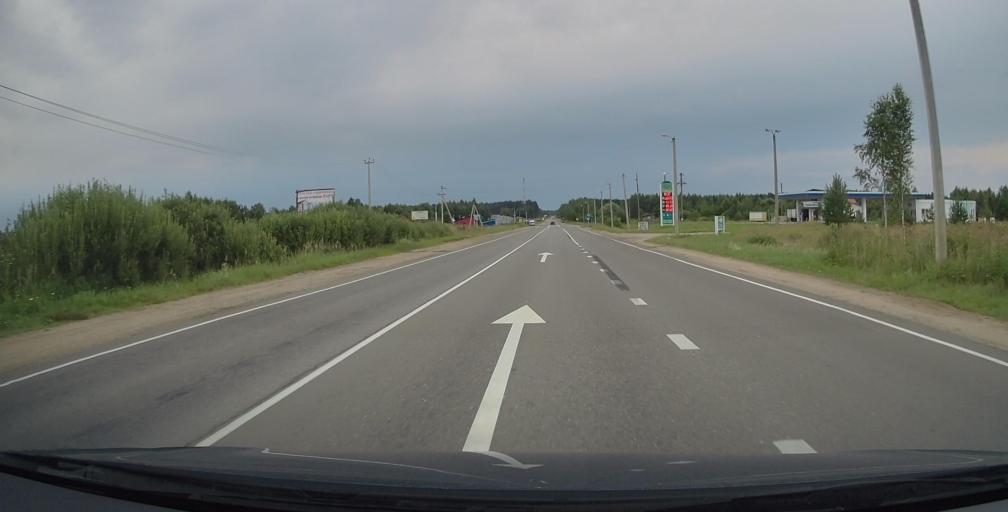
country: RU
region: Tverskaya
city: Kalyazin
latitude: 57.0286
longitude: 37.9812
